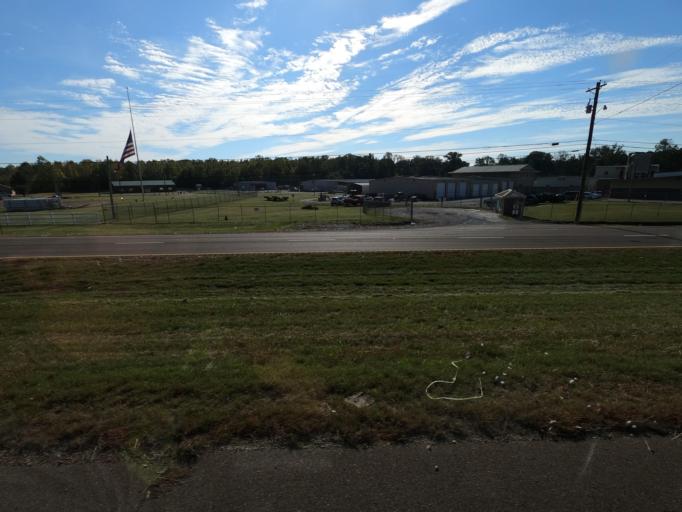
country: US
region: Tennessee
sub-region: Tipton County
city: Munford
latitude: 35.4131
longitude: -89.8296
